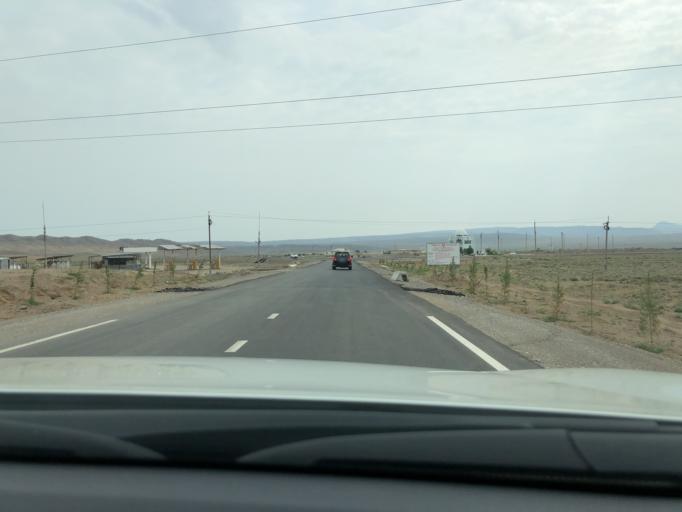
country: TJ
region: Viloyati Sughd
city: Kim
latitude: 40.1989
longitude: 70.4805
